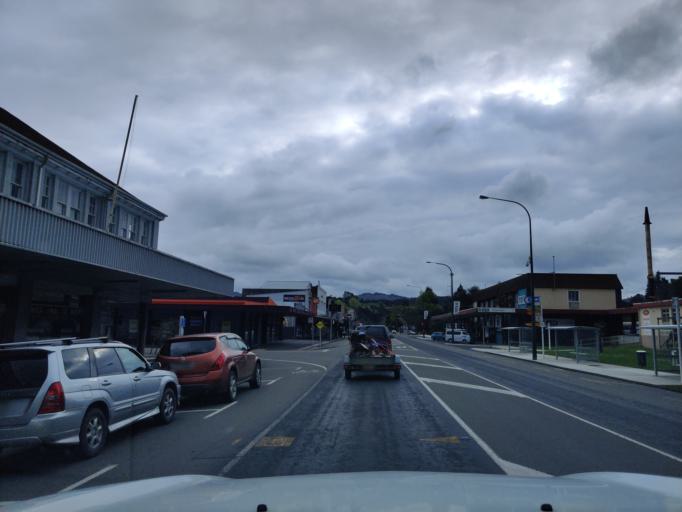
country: NZ
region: Waikato
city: Turangi
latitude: -38.8830
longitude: 175.2659
